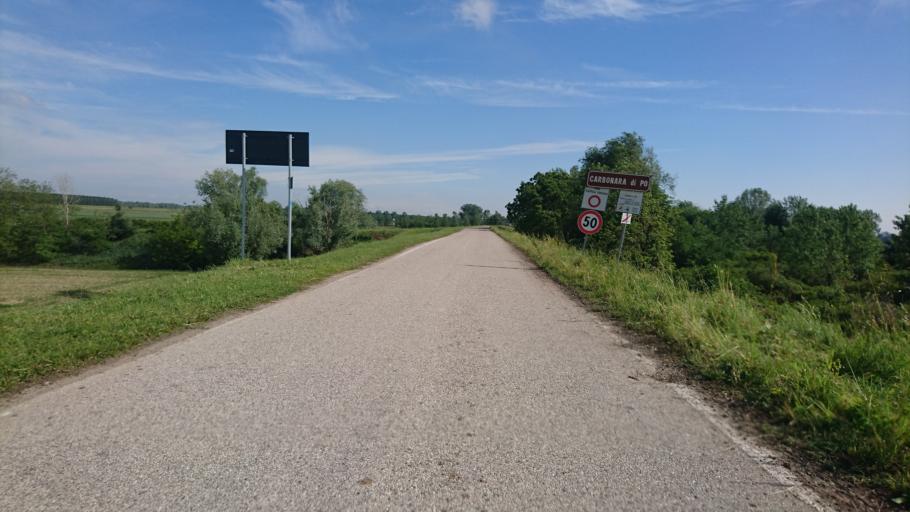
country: IT
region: Lombardy
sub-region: Provincia di Mantova
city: Carbonara di Po
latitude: 45.0310
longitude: 11.2584
